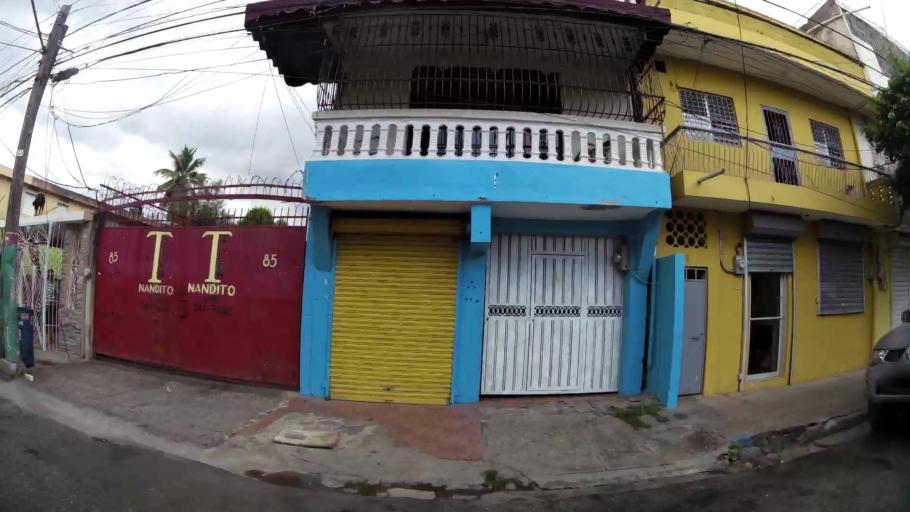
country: DO
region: Nacional
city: La Agustina
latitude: 18.4915
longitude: -69.9170
